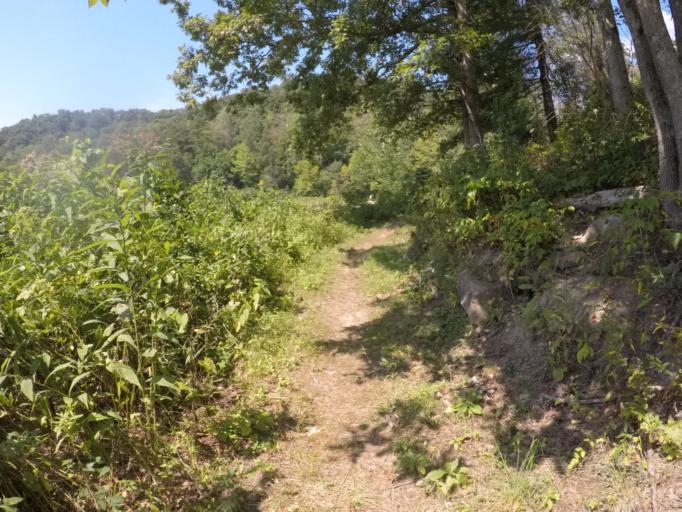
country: US
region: Ohio
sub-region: Lawrence County
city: Ironton
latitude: 38.6195
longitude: -82.6275
